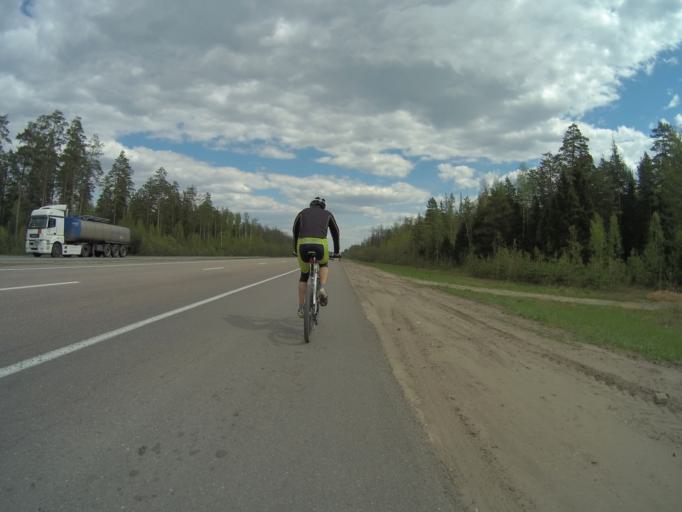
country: RU
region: Vladimir
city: Bogolyubovo
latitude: 56.0939
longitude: 40.5441
